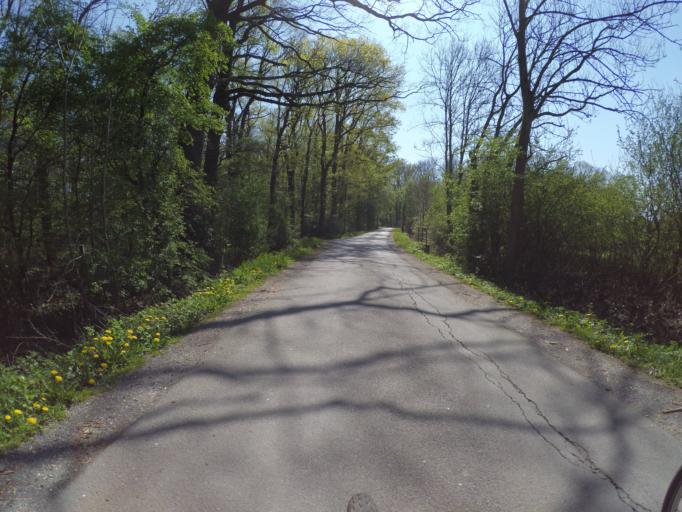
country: DE
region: North Rhine-Westphalia
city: Ludinghausen
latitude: 51.7593
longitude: 7.4396
